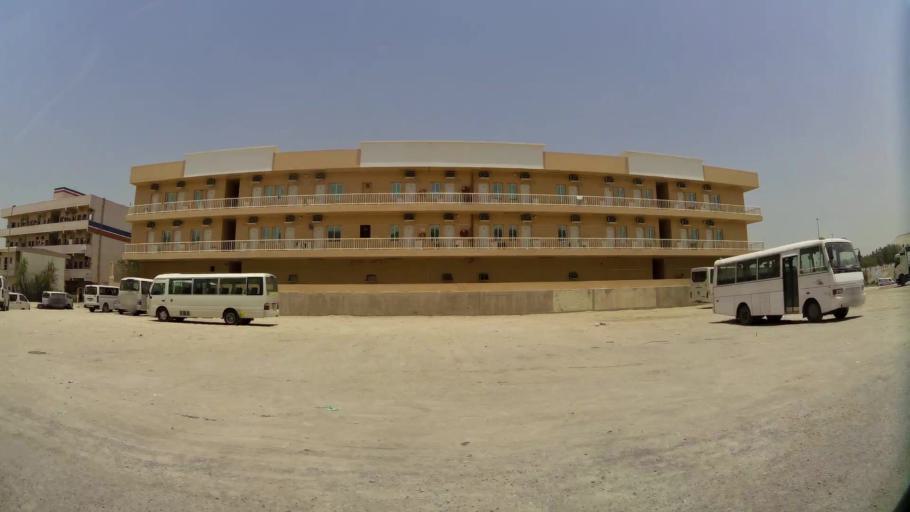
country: AE
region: Ash Shariqah
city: Sharjah
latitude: 25.2764
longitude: 55.4250
